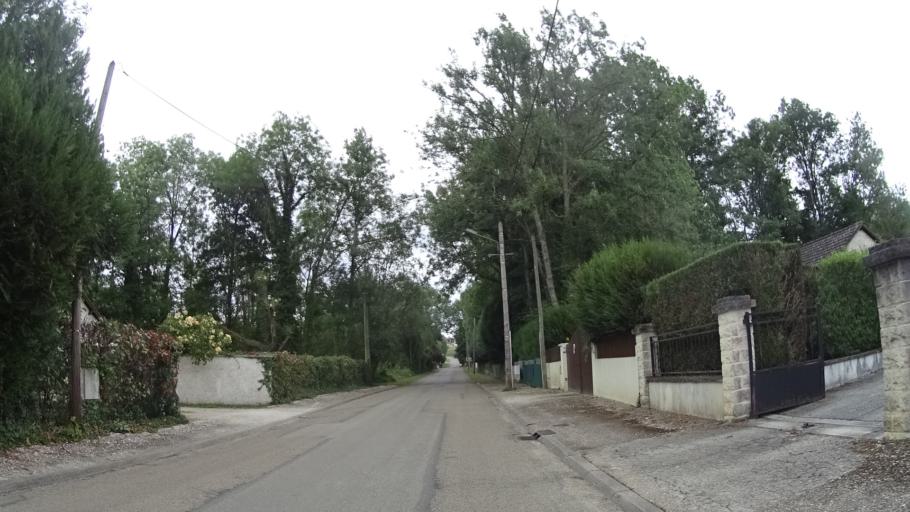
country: FR
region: Bourgogne
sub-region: Departement de l'Yonne
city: Cezy
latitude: 47.9556
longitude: 3.3639
